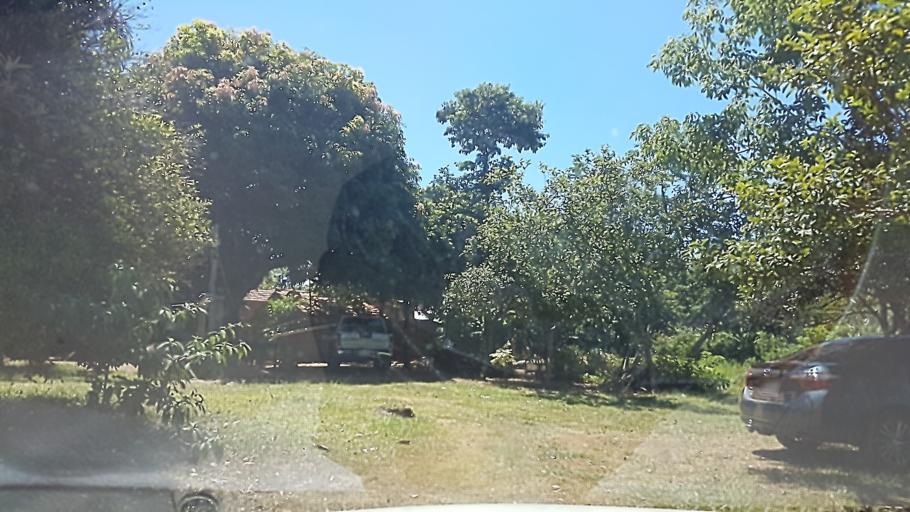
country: PY
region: Itapua
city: San Cosme y Damian
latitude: -27.3261
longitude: -56.3240
